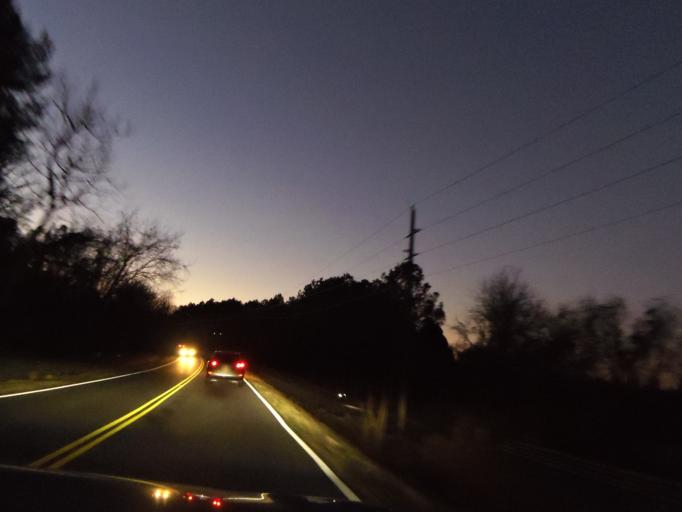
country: US
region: Virginia
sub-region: Henrico County
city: Montrose
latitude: 37.5020
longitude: -77.4094
